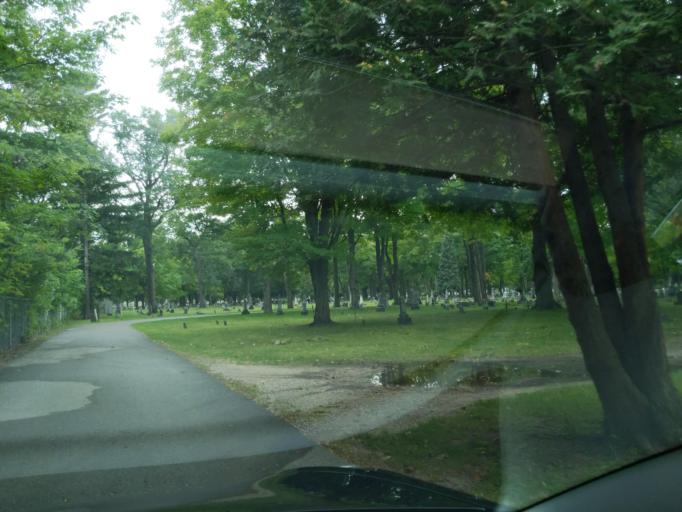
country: US
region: Michigan
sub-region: Grand Traverse County
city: Traverse City
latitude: 44.7560
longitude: -85.5851
